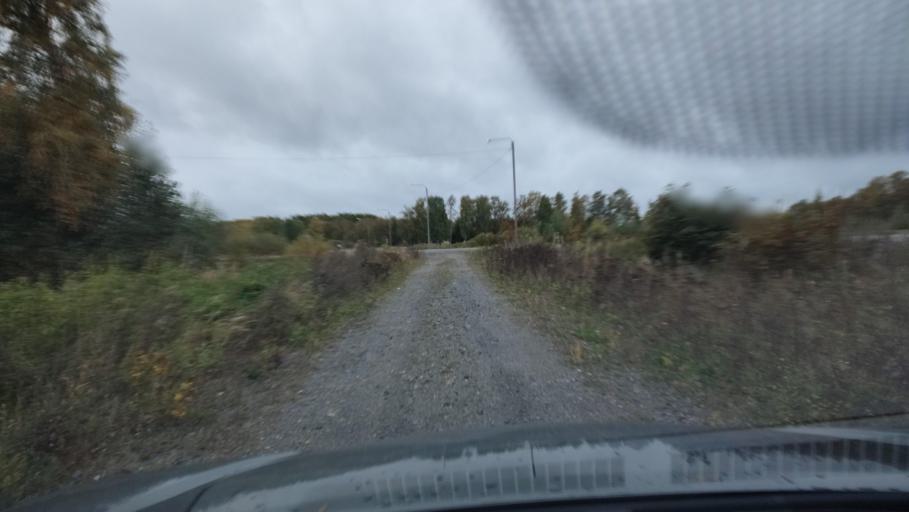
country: FI
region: Ostrobothnia
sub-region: Sydosterbotten
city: Kristinestad
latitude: 62.2783
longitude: 21.4083
